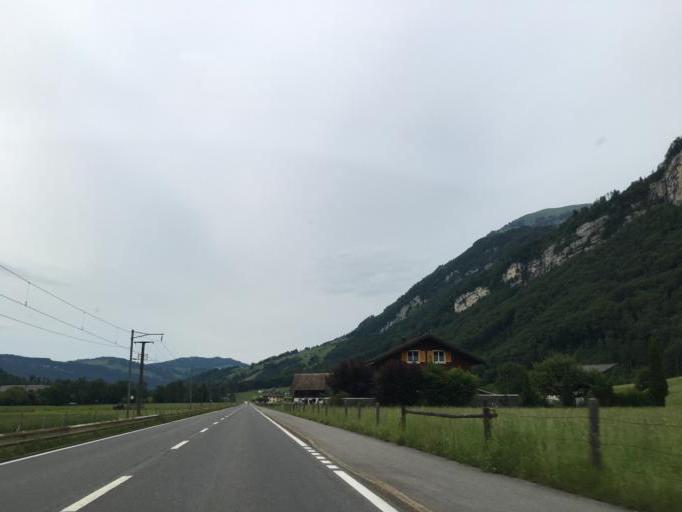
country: CH
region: Nidwalden
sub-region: Nidwalden
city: Wolfenschiessen
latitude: 46.9139
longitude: 8.3961
